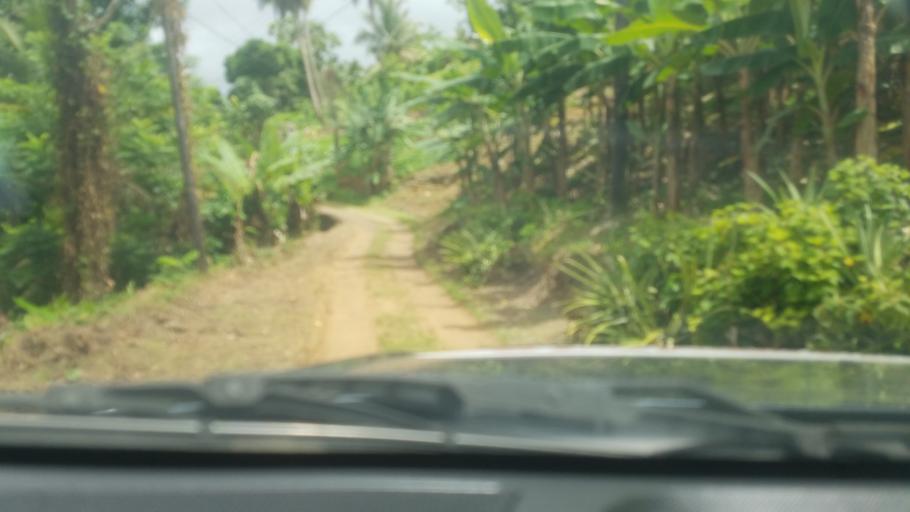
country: LC
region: Micoud Quarter
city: Micoud
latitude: 13.8023
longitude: -60.9509
